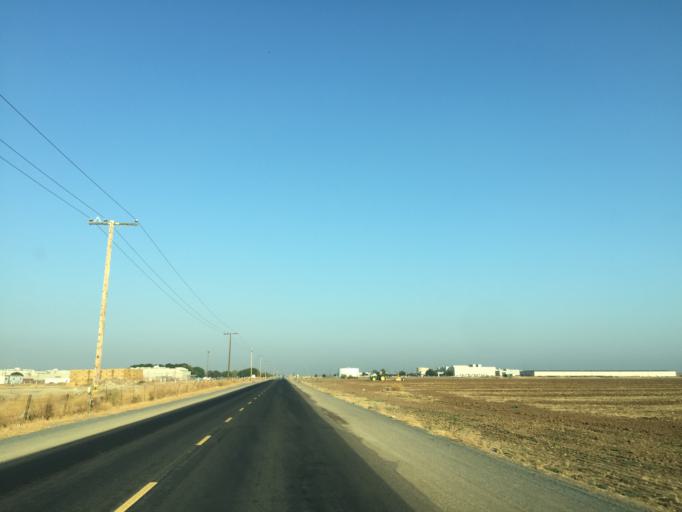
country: US
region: California
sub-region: Tulare County
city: Cutler
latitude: 36.4580
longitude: -119.3154
